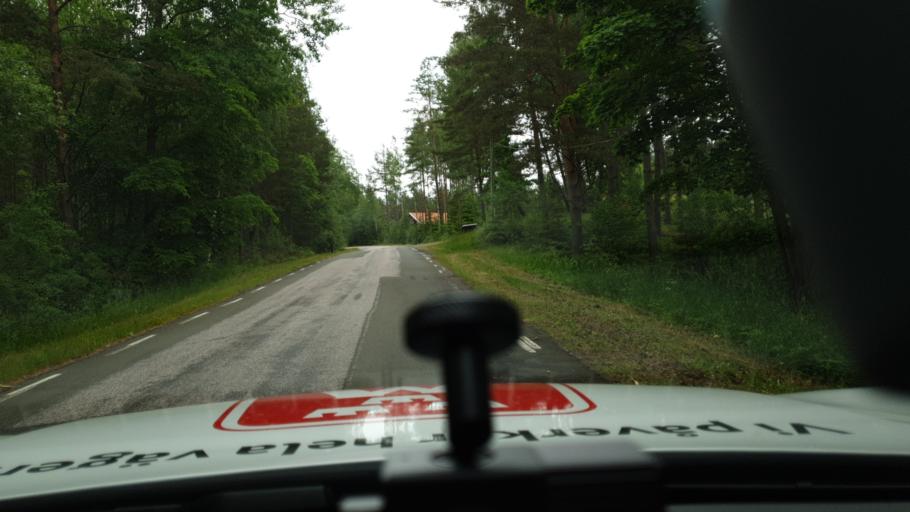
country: SE
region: Vaestra Goetaland
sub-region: Karlsborgs Kommun
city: Molltorp
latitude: 58.4225
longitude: 14.3674
